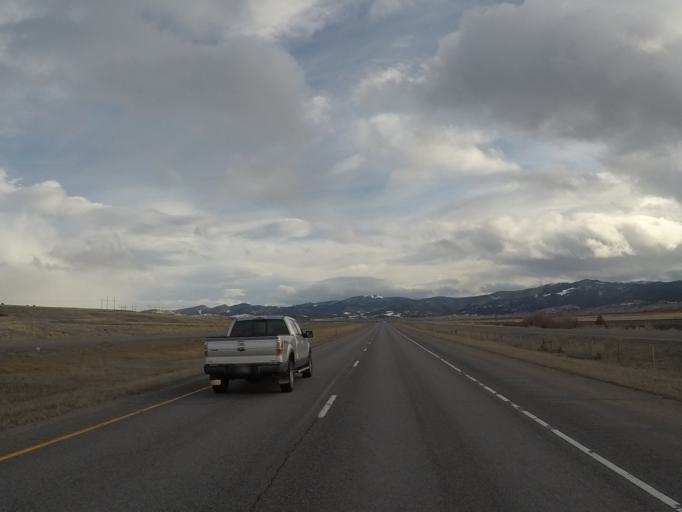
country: US
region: Montana
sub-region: Deer Lodge County
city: Warm Springs
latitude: 46.1219
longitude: -112.7992
